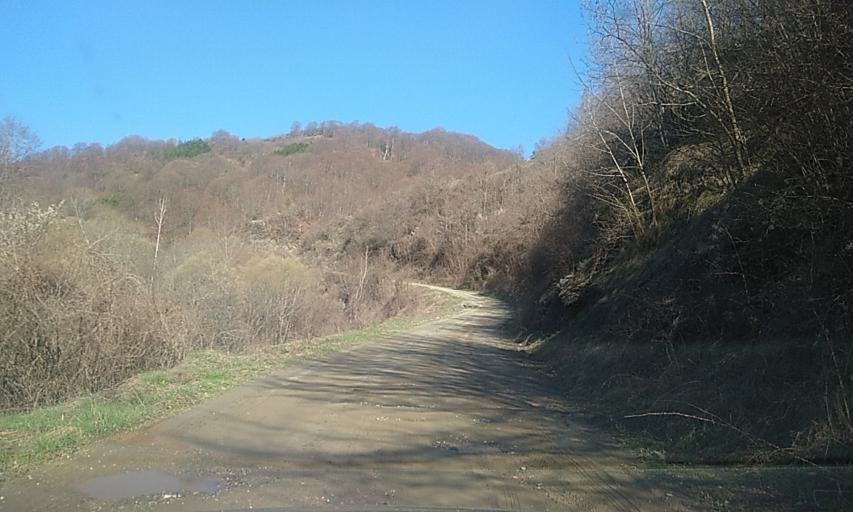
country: MK
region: Kriva Palanka
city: Kriva Palanka
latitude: 42.3413
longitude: 22.3673
